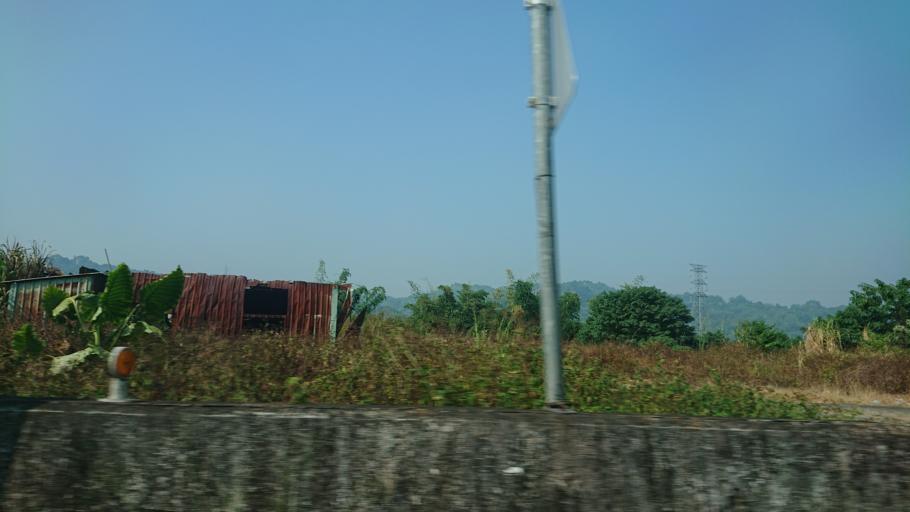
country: TW
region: Taiwan
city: Lugu
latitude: 23.7078
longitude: 120.6639
